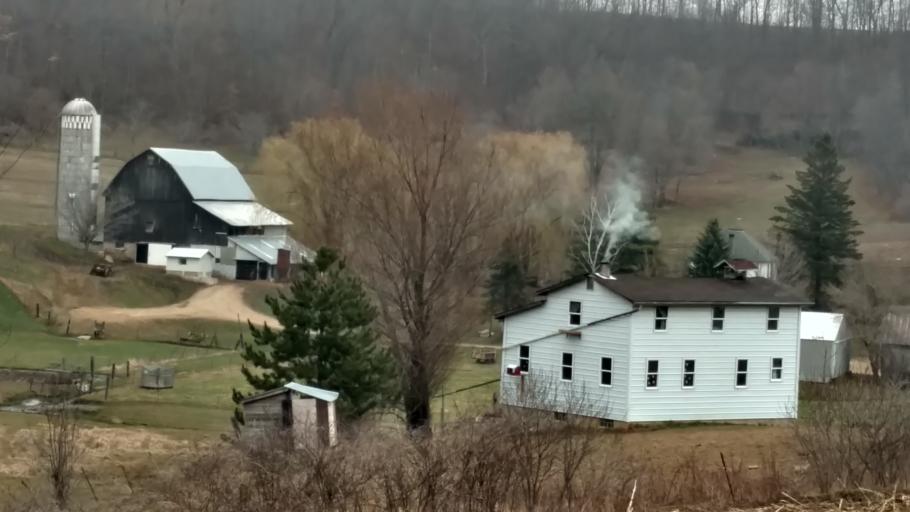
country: US
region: Wisconsin
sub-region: Vernon County
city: Hillsboro
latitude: 43.6193
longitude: -90.4064
